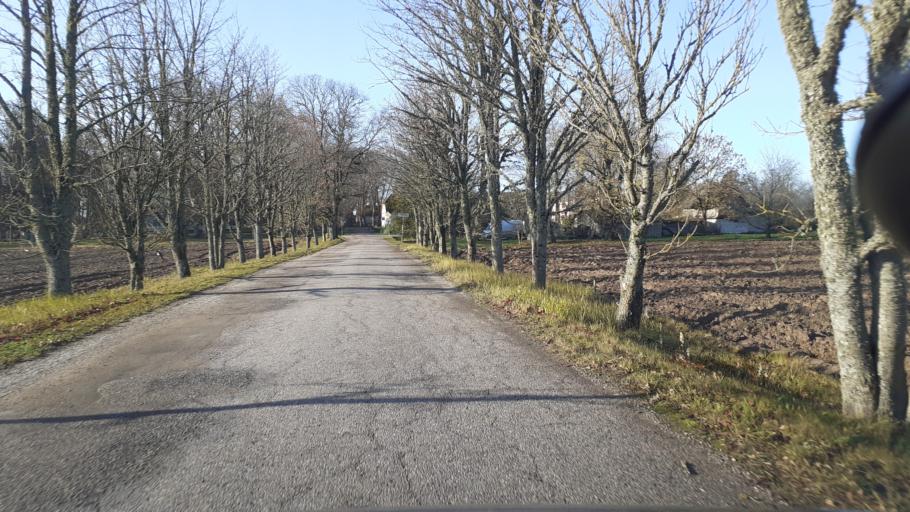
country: LV
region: Kuldigas Rajons
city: Kuldiga
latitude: 57.0006
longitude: 21.8905
